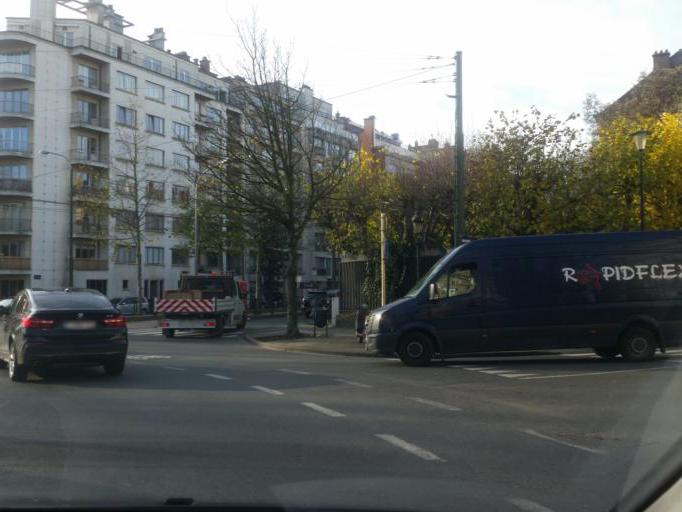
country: BE
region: Brussels Capital
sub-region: Bruxelles-Capitale
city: Brussels
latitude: 50.8122
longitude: 4.3537
